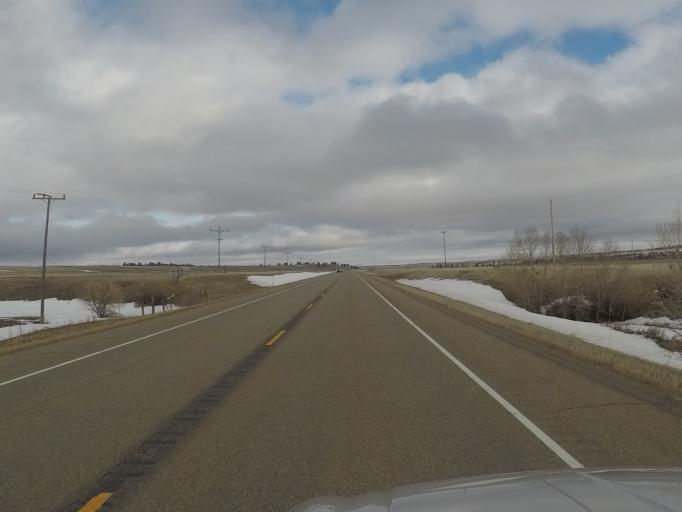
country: US
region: Montana
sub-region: Golden Valley County
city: Ryegate
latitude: 46.3254
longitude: -109.4569
